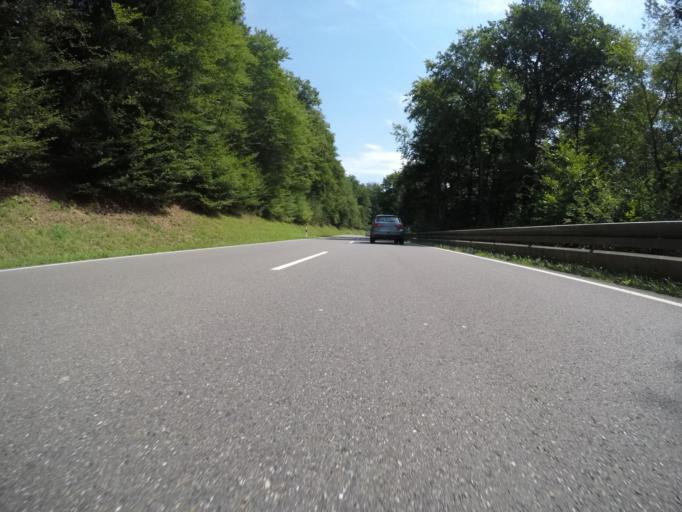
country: DE
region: Baden-Wuerttemberg
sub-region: Regierungsbezirk Stuttgart
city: Gerlingen
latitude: 48.7611
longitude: 9.0605
